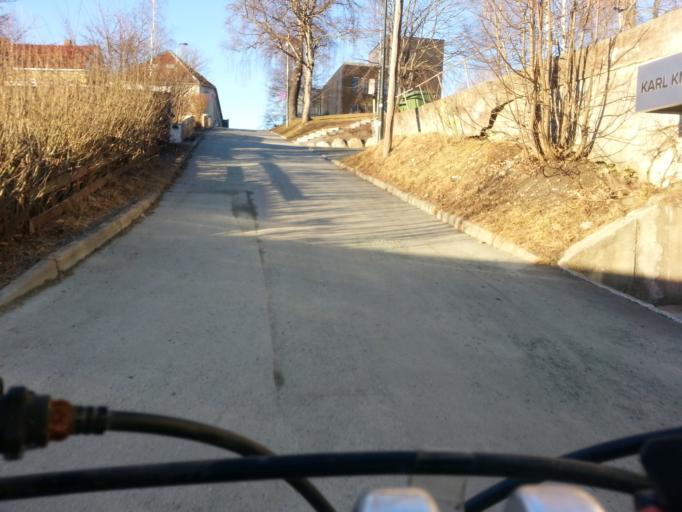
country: NO
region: Sor-Trondelag
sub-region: Trondheim
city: Trondheim
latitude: 63.4279
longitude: 10.3850
